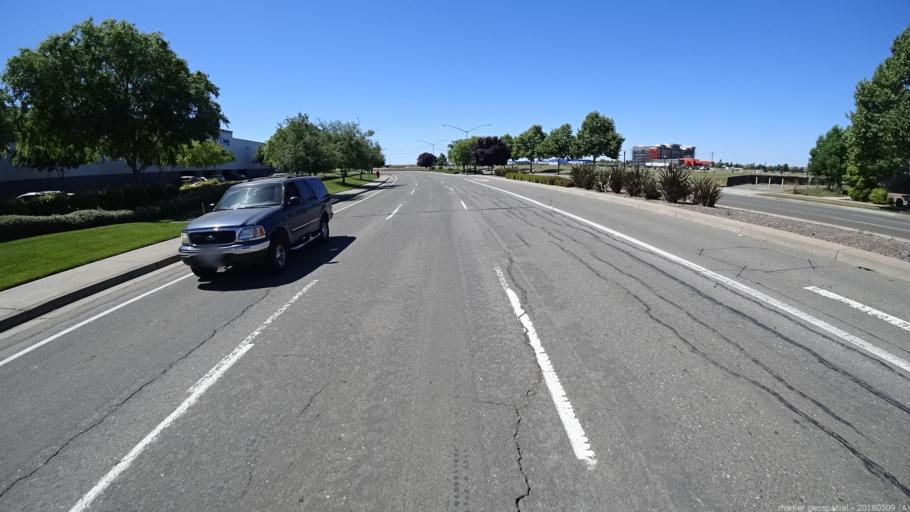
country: US
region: California
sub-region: Yolo County
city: West Sacramento
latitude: 38.6524
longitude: -121.5260
